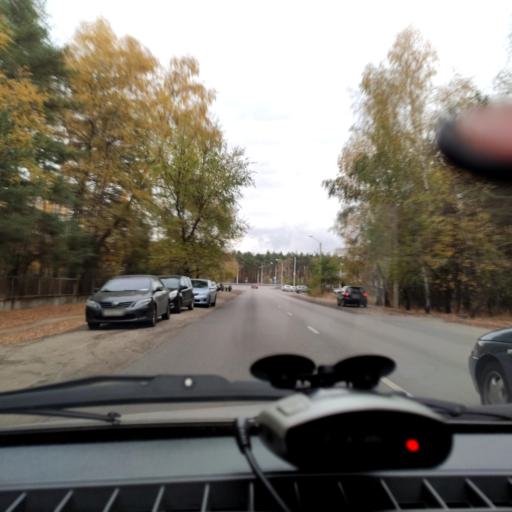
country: RU
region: Voronezj
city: Podgornoye
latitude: 51.7383
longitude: 39.1785
